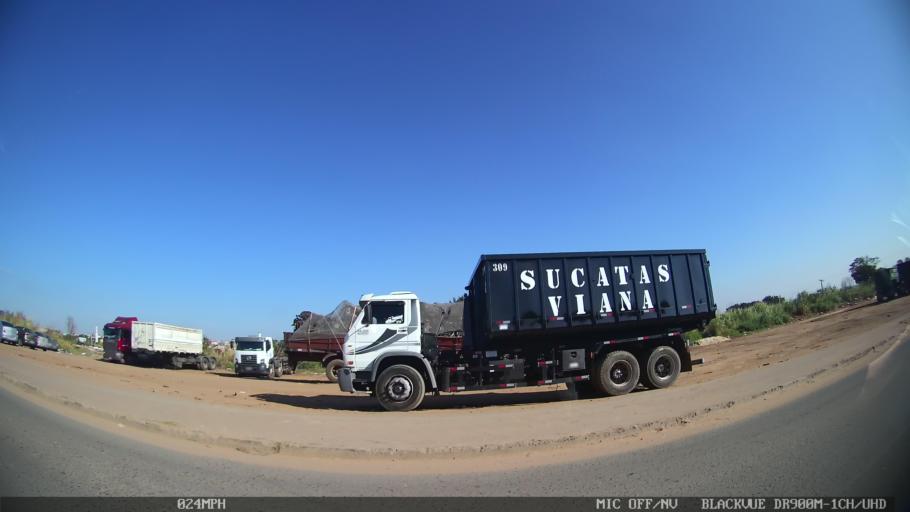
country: BR
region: Sao Paulo
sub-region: Campinas
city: Campinas
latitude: -22.9833
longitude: -47.1095
